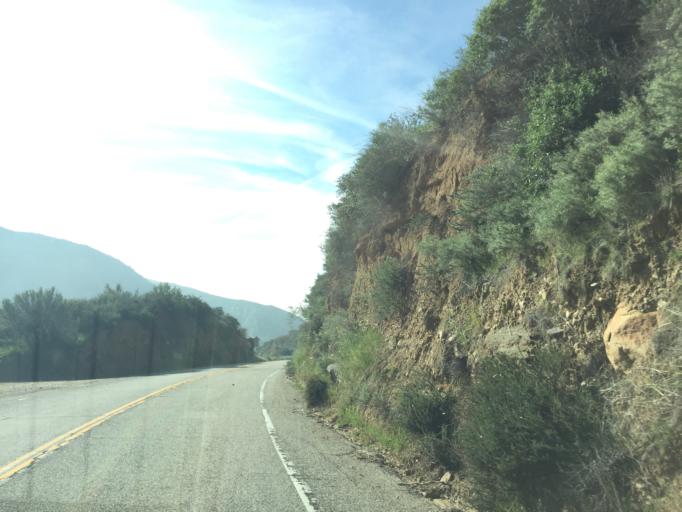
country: US
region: California
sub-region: San Bernardino County
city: San Antonio Heights
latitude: 34.1784
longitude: -117.6769
